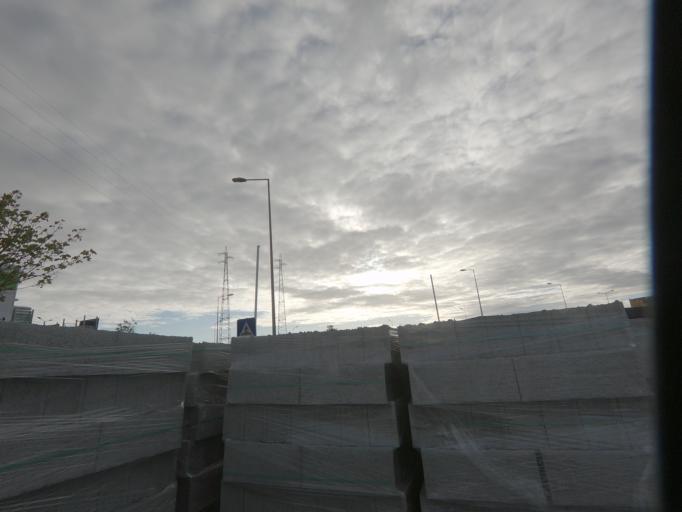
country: PT
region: Porto
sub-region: Matosinhos
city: Santa Cruz do Bispo
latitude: 41.2110
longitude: -8.6851
